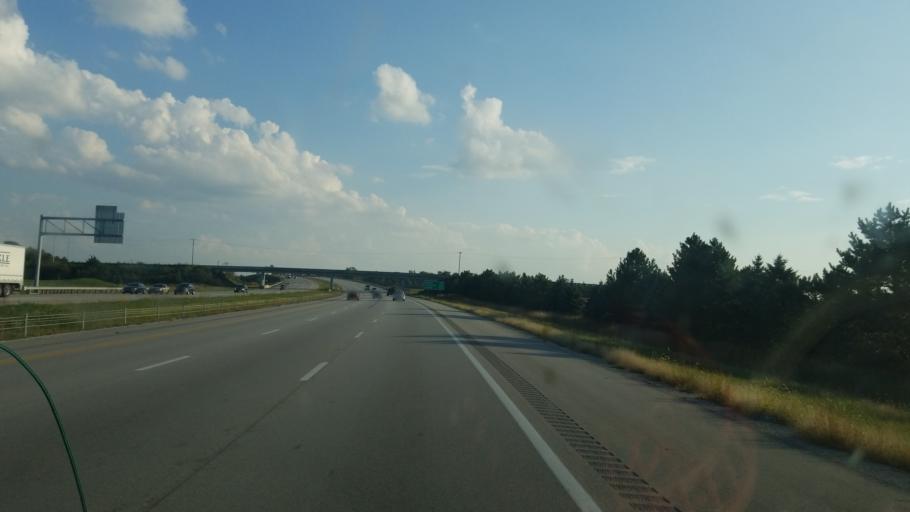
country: US
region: Ohio
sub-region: Wood County
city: Bowling Green
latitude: 41.4458
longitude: -83.6224
